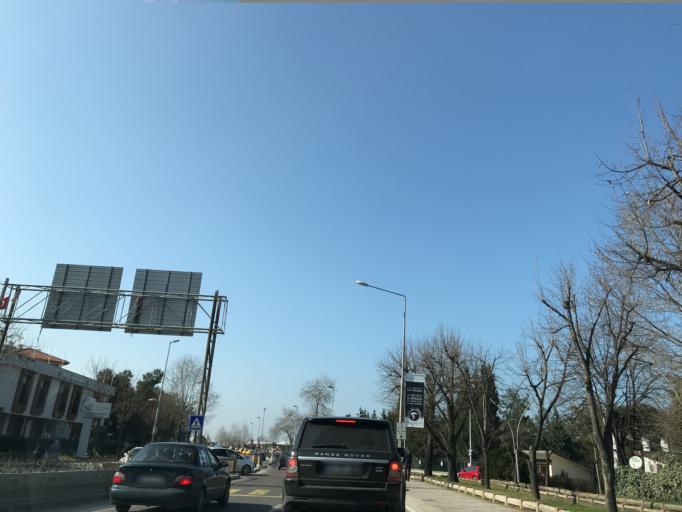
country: TR
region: Yalova
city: Yalova
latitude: 40.6584
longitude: 29.2815
